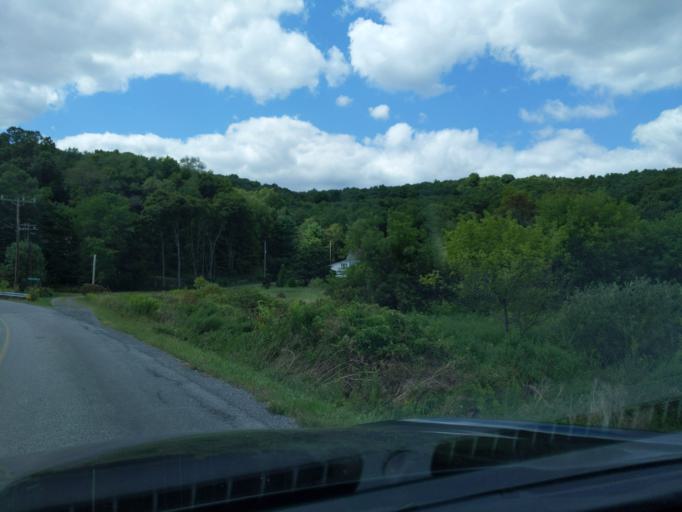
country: US
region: Pennsylvania
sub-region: Blair County
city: Tyrone
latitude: 40.7055
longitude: -78.2142
